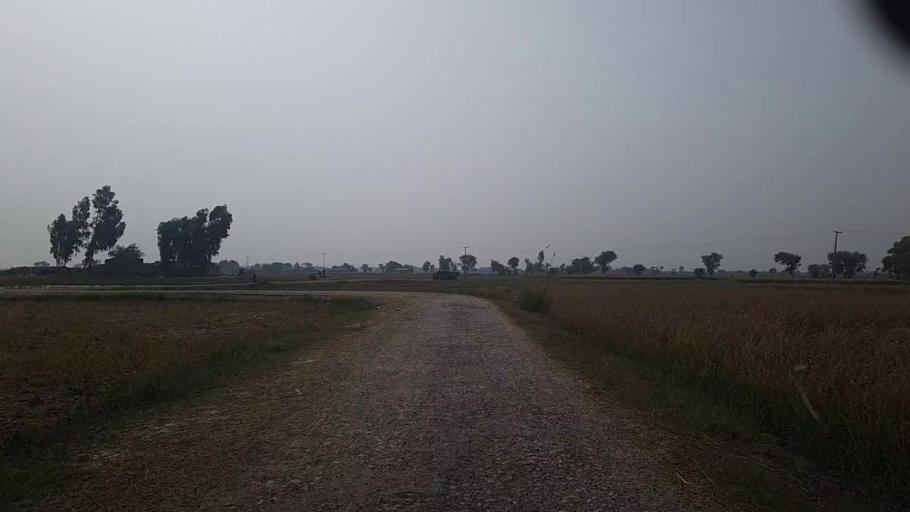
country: PK
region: Sindh
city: Kashmor
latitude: 28.3919
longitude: 69.4229
